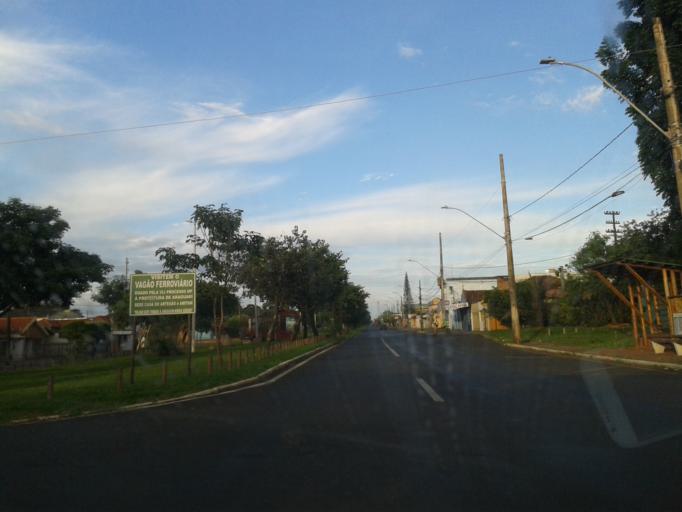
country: BR
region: Minas Gerais
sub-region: Araguari
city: Araguari
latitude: -18.6407
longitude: -48.1936
